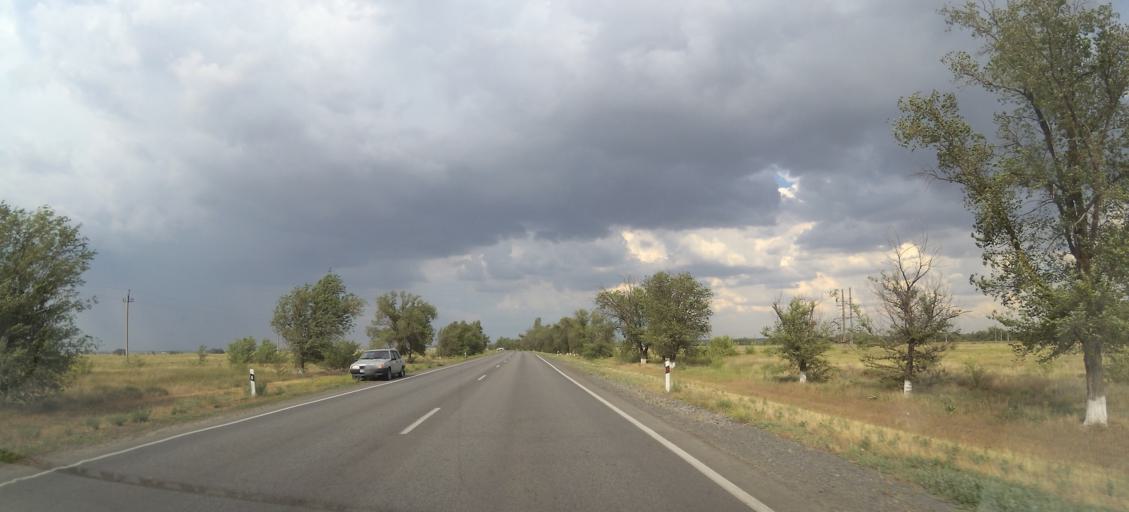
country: RU
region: Rostov
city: Zimovniki
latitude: 47.1302
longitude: 42.4161
